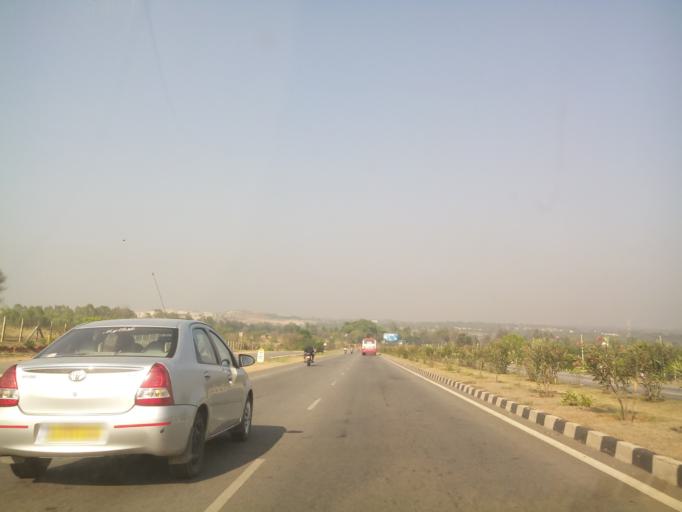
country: IN
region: Karnataka
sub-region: Bangalore Rural
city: Nelamangala
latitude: 13.0611
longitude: 77.3405
